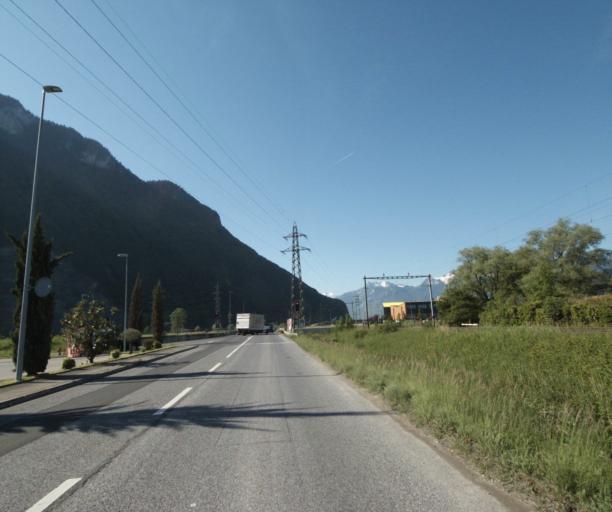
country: CH
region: Vaud
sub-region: Aigle District
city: Villeneuve
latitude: 46.3853
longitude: 6.9288
